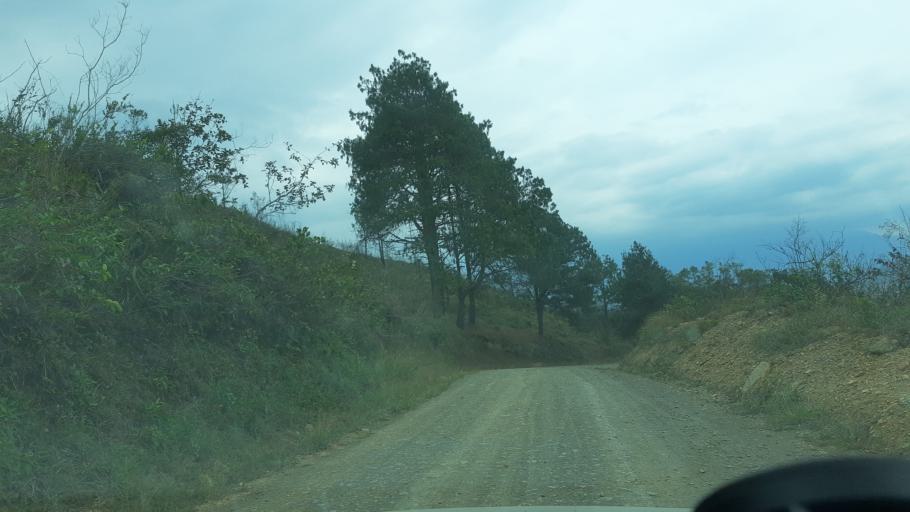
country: CO
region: Boyaca
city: Somondoco
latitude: 4.9844
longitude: -73.3761
